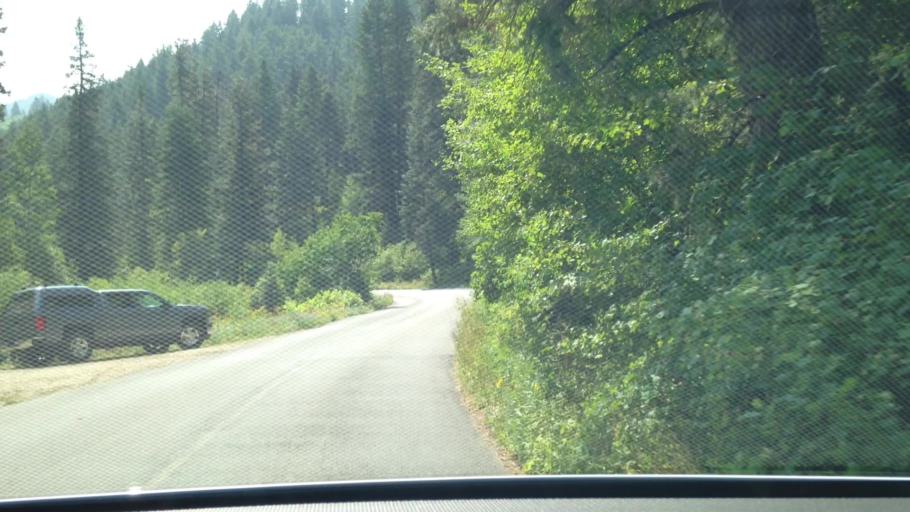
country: US
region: Utah
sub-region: Summit County
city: Summit Park
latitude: 40.7010
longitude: -111.6869
